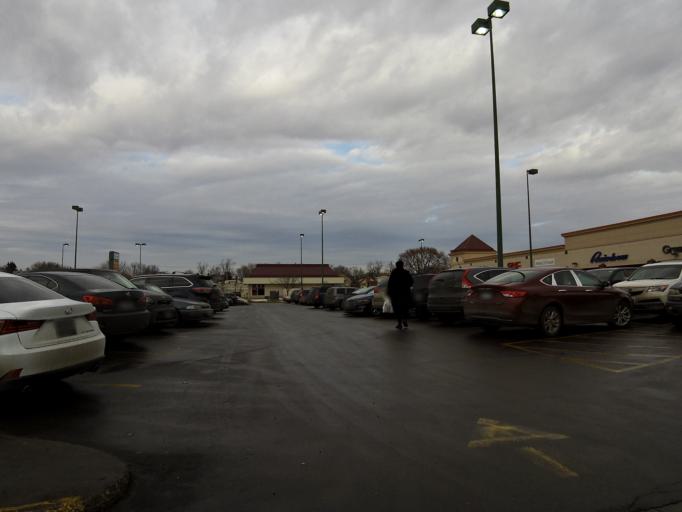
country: US
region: Minnesota
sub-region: Ramsey County
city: Falcon Heights
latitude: 44.9544
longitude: -93.1632
